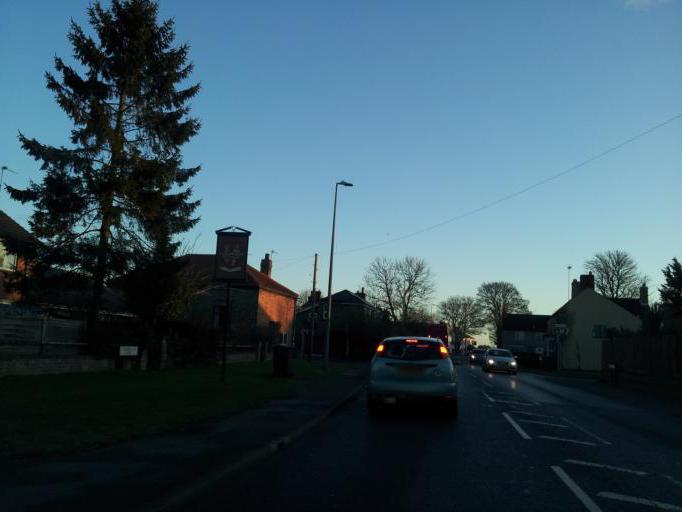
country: GB
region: England
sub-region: Lincolnshire
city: Sudbrooke
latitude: 53.2744
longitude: -0.4083
